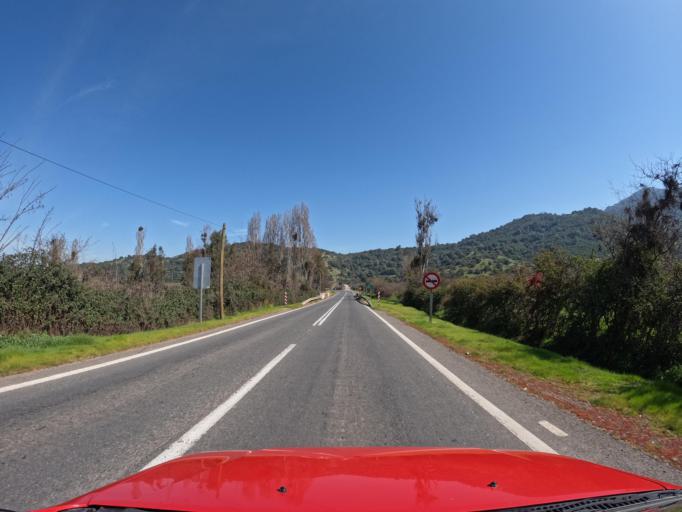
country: CL
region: Maule
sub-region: Provincia de Curico
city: Rauco
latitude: -34.9810
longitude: -71.4175
